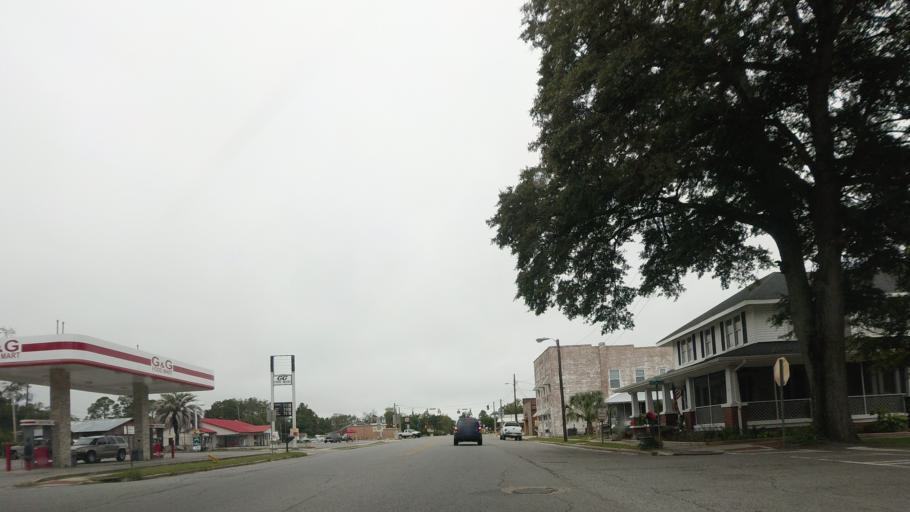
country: US
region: Georgia
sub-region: Irwin County
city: Ocilla
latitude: 31.5931
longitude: -83.2505
